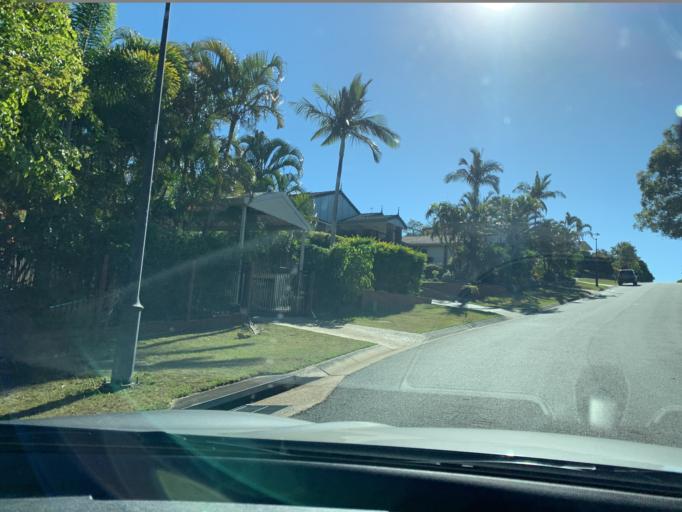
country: AU
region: Queensland
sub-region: Brisbane
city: Wynnum
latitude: -27.4289
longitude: 153.1606
